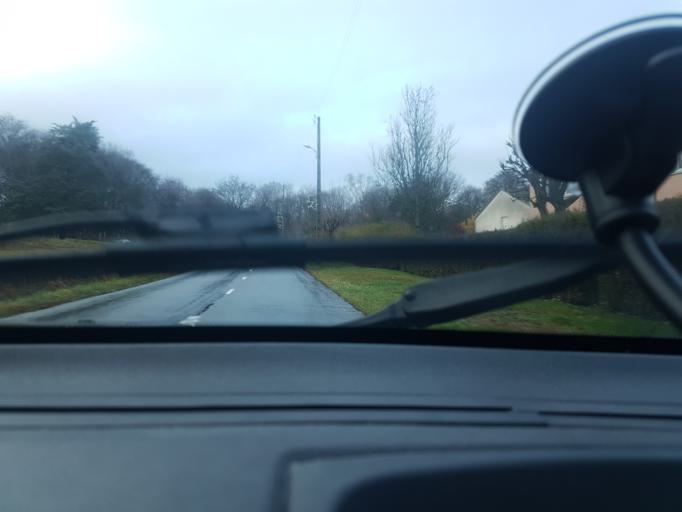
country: FR
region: Franche-Comte
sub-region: Territoire de Belfort
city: Bavilliers
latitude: 47.6075
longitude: 6.8428
